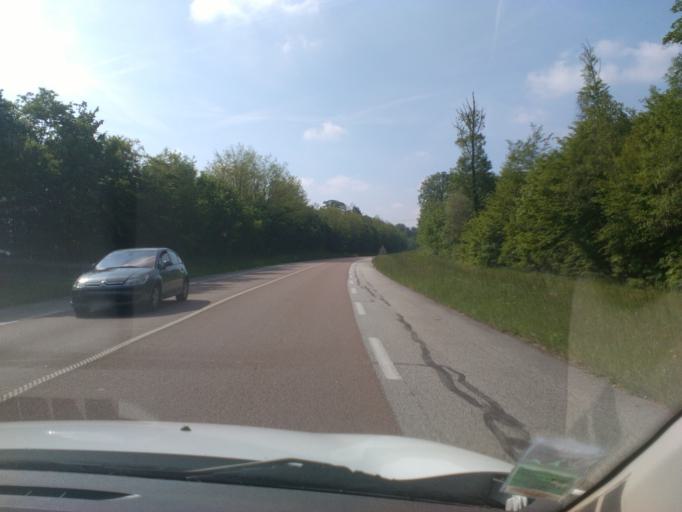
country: FR
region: Lorraine
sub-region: Departement des Vosges
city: Les Forges
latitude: 48.1960
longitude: 6.3986
